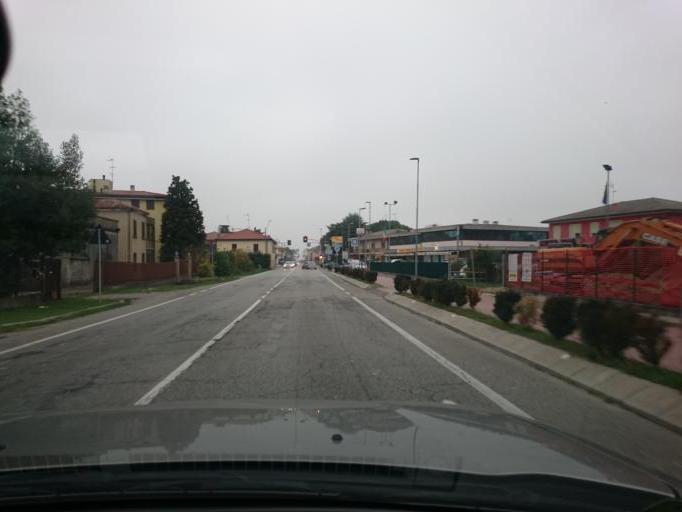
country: IT
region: Veneto
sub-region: Provincia di Padova
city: Legnaro
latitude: 45.3430
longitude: 11.9679
